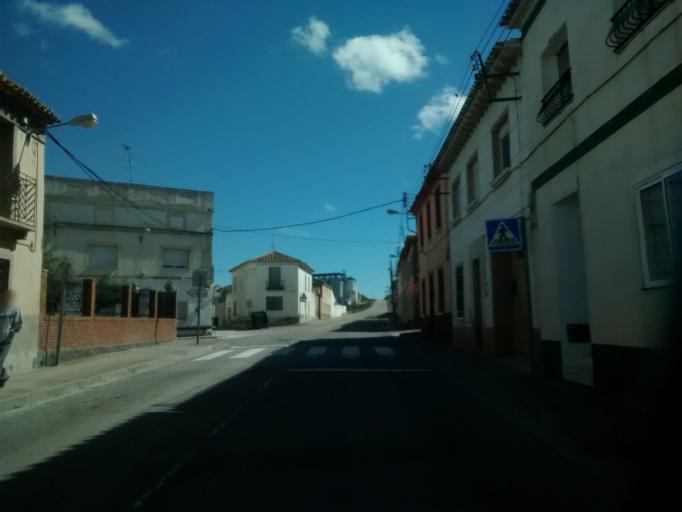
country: ES
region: Aragon
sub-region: Provincia de Zaragoza
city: Lecinena
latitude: 41.7988
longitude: -0.6089
